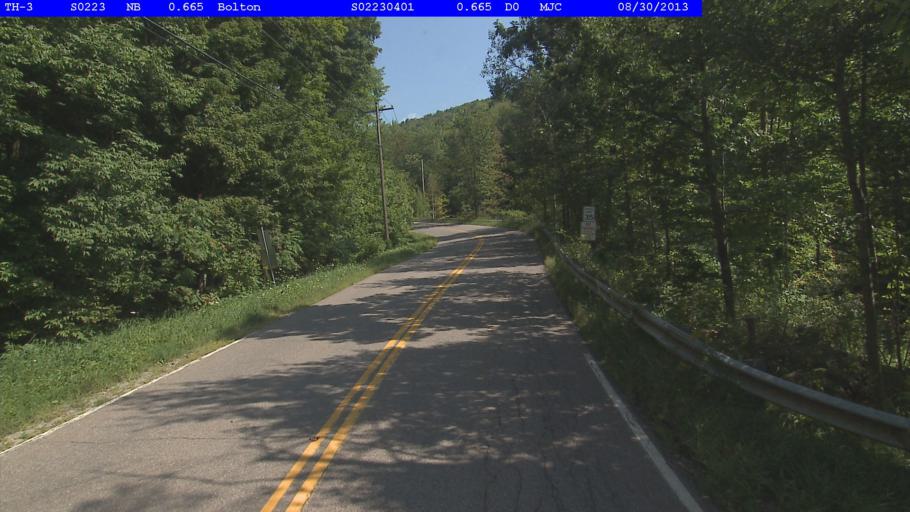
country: US
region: Vermont
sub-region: Washington County
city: Waterbury
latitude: 44.3806
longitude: -72.8758
